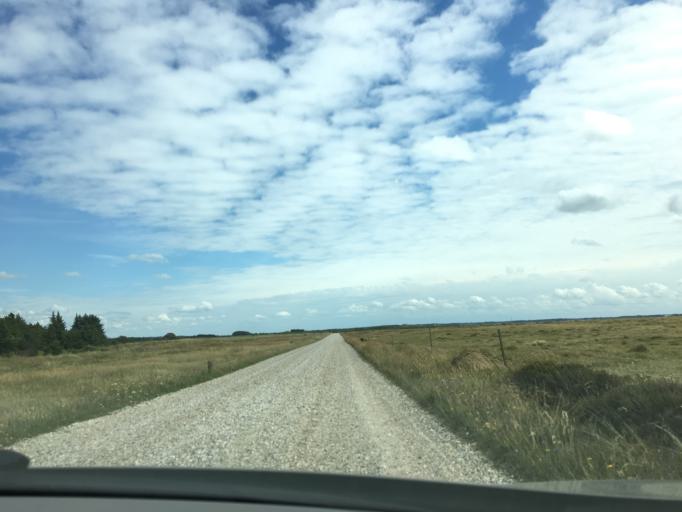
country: DK
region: South Denmark
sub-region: Varde Kommune
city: Oksbol
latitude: 55.7232
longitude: 8.2024
